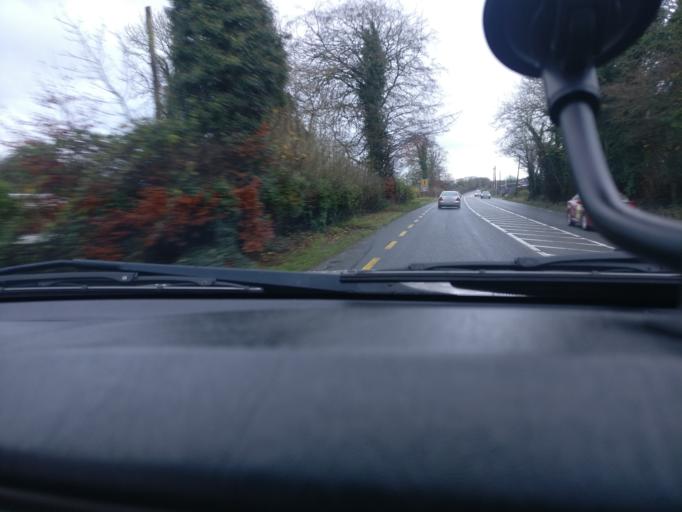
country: IE
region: Leinster
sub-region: Kildare
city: Kilcock
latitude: 53.4208
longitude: -6.7392
